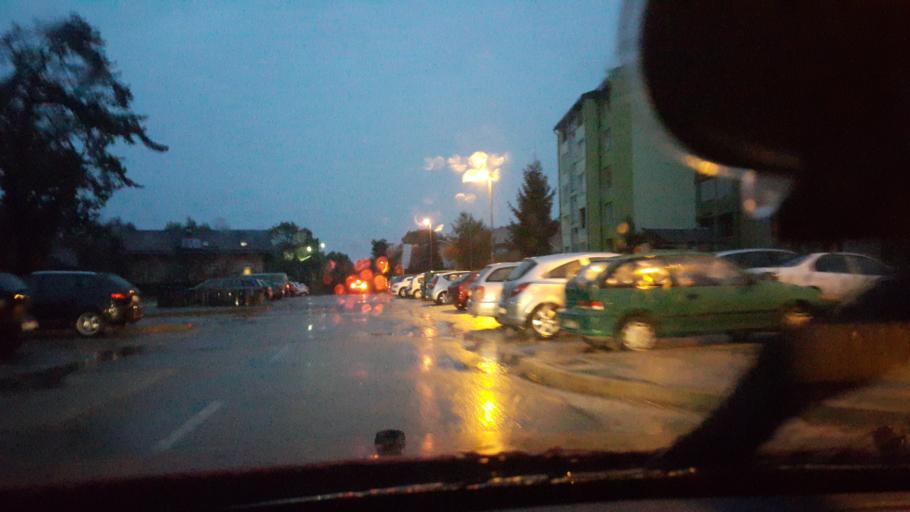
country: SI
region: Miklavz na Dravskem Polju
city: Miklavz na Dravskem Polju
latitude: 46.5293
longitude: 15.6818
